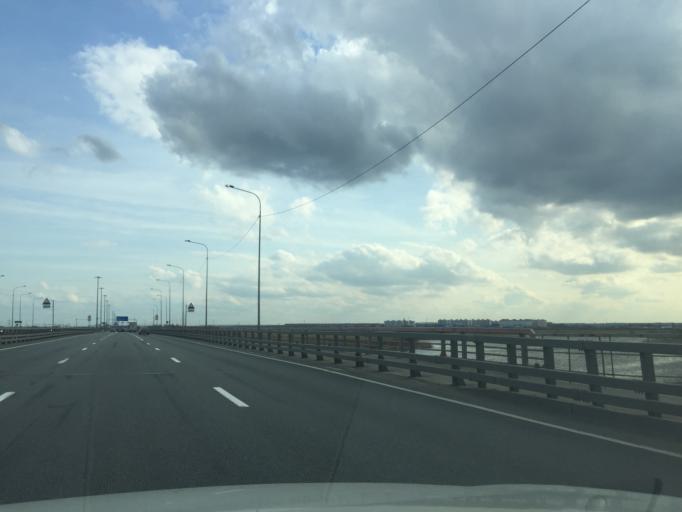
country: RU
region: St.-Petersburg
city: Petro-Slavyanka
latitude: 59.7848
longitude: 30.4962
